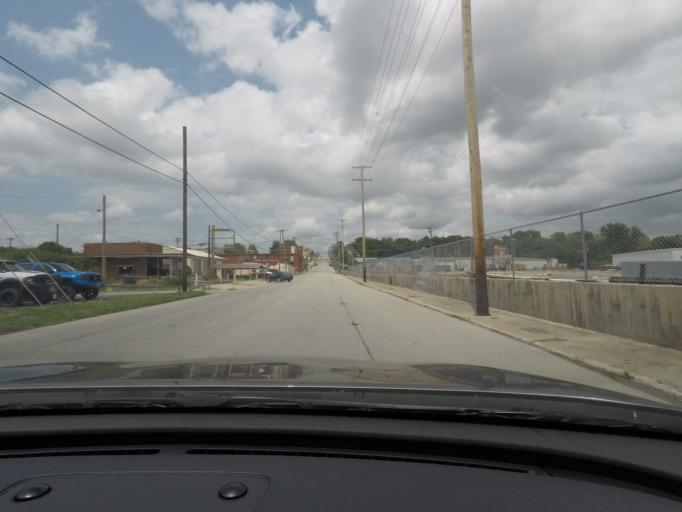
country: US
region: Missouri
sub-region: Carroll County
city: Carrollton
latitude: 39.3515
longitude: -93.4960
